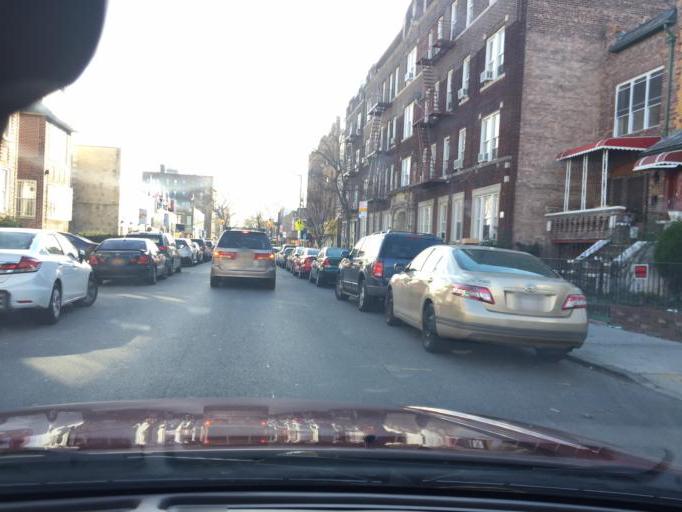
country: US
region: New York
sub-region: Kings County
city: Brooklyn
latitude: 40.6258
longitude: -73.9625
